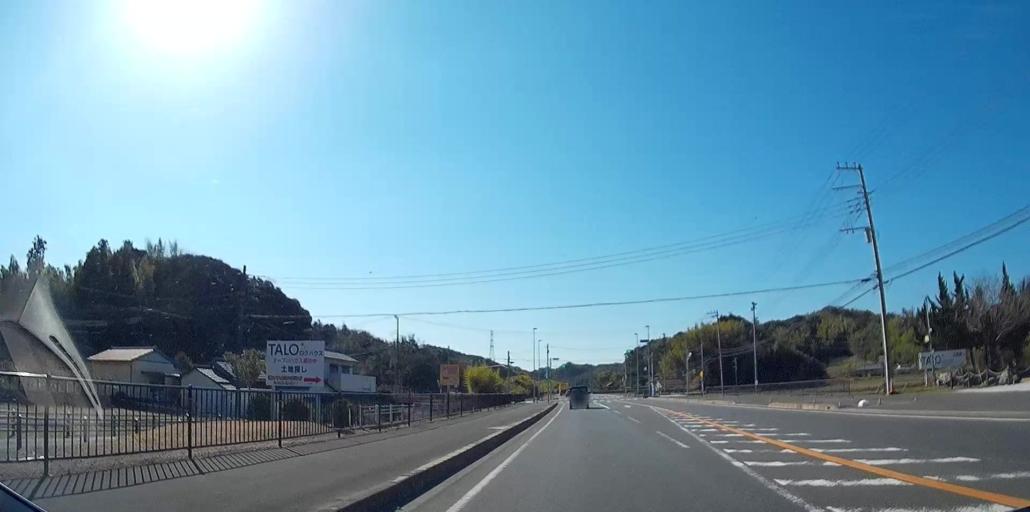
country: JP
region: Chiba
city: Kimitsu
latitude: 35.2955
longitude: 139.9167
